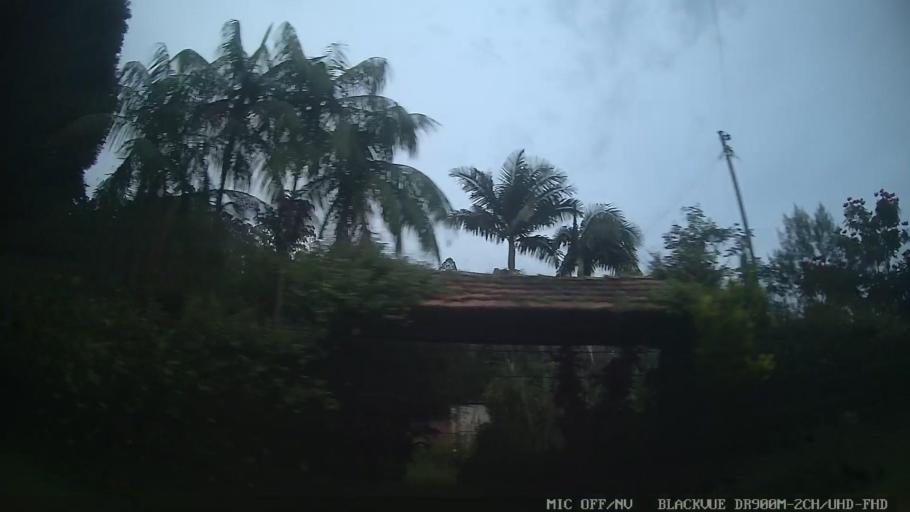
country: BR
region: Sao Paulo
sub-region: Rio Grande Da Serra
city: Rio Grande da Serra
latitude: -23.6830
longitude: -46.3015
